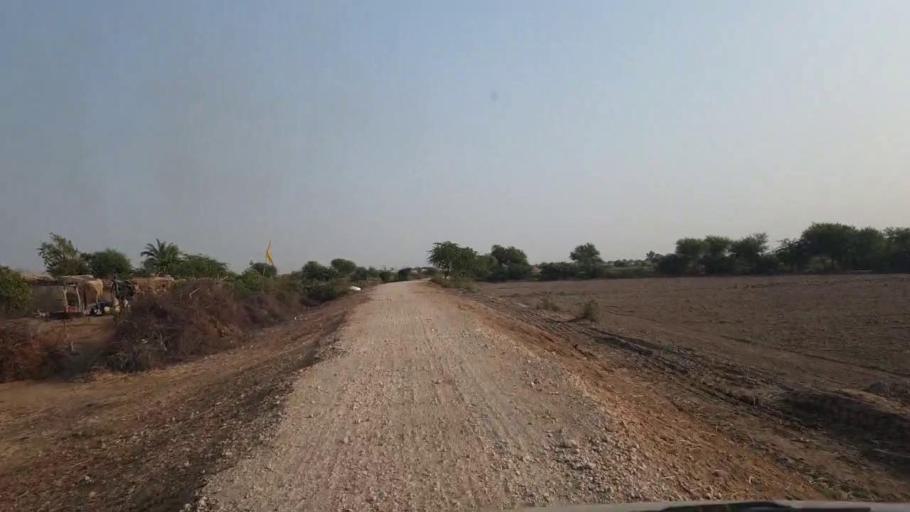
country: PK
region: Sindh
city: Rajo Khanani
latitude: 25.0230
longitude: 68.7811
